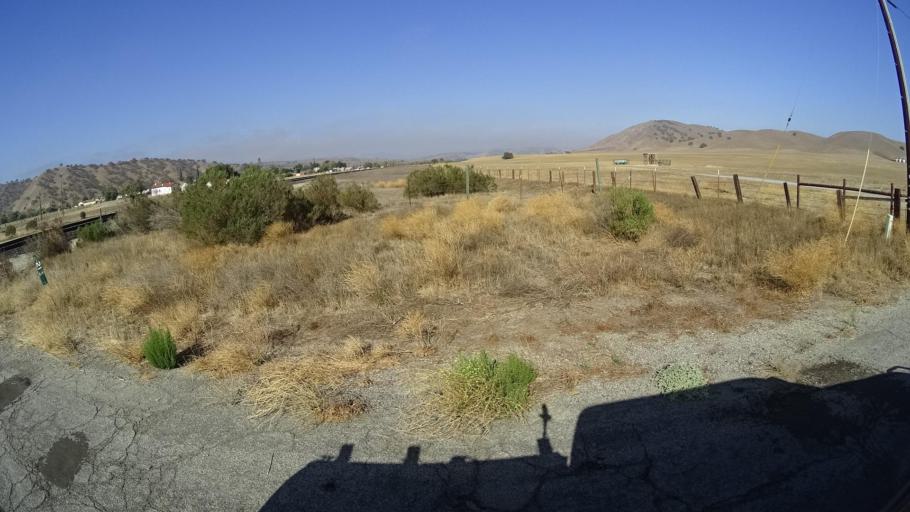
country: US
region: California
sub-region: San Luis Obispo County
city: San Miguel
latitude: 35.8642
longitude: -120.7956
